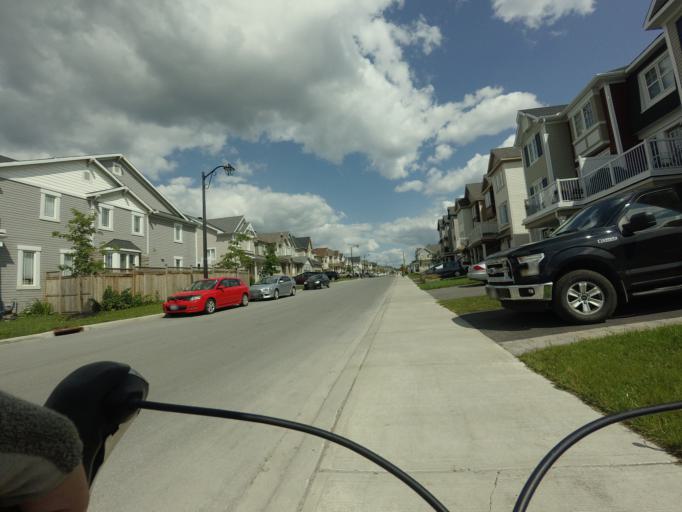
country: CA
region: Ontario
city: Bells Corners
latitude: 45.2748
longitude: -75.8460
